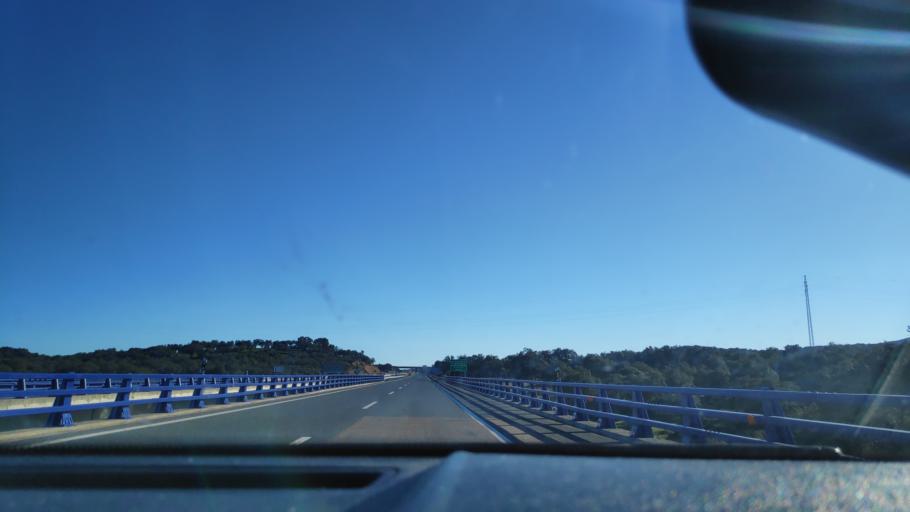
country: ES
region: Andalusia
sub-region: Provincia de Huelva
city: Santa Olalla del Cala
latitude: 37.9586
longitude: -6.2331
